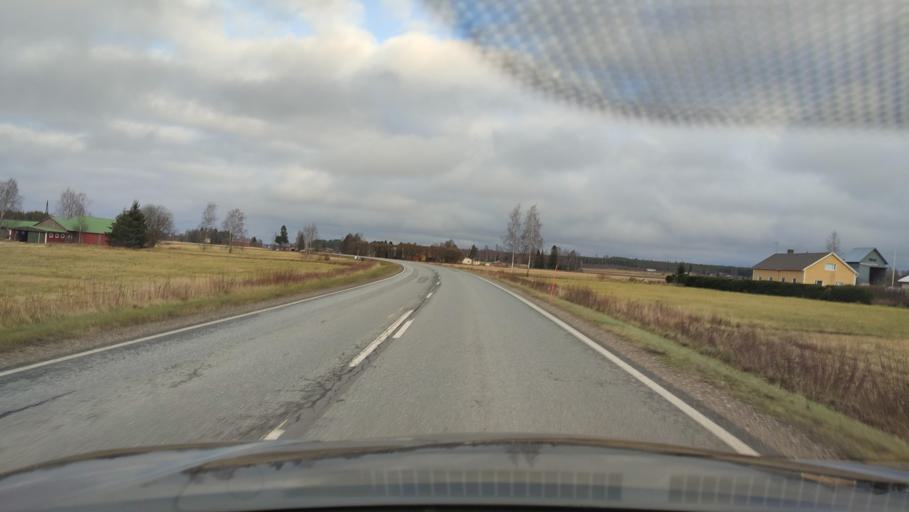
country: FI
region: Southern Ostrobothnia
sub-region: Suupohja
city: Kauhajoki
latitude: 62.3583
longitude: 22.0680
